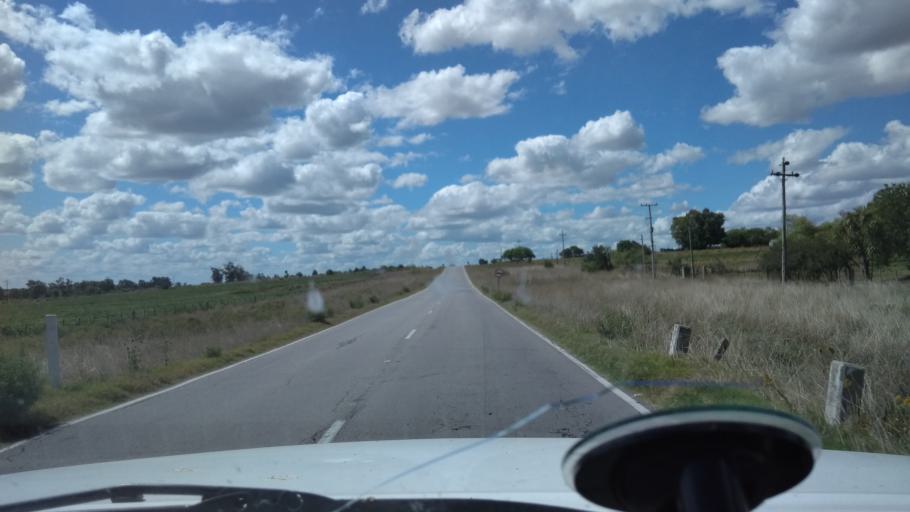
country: UY
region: Canelones
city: San Ramon
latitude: -34.3539
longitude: -55.9595
